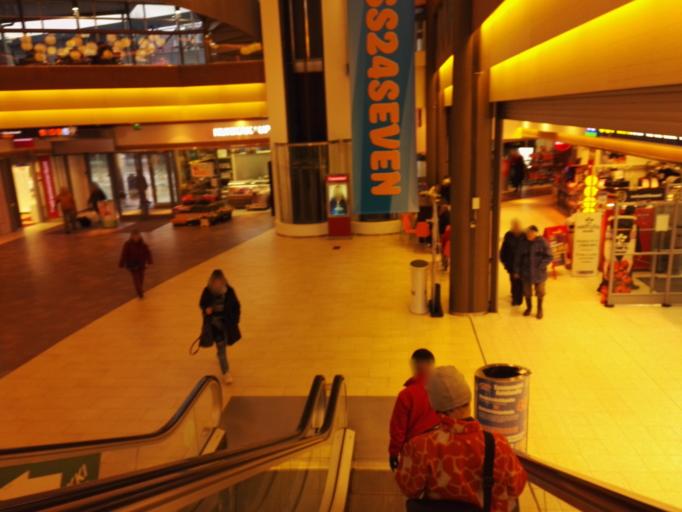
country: FI
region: Uusimaa
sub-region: Helsinki
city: Espoo
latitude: 60.2046
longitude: 24.6566
